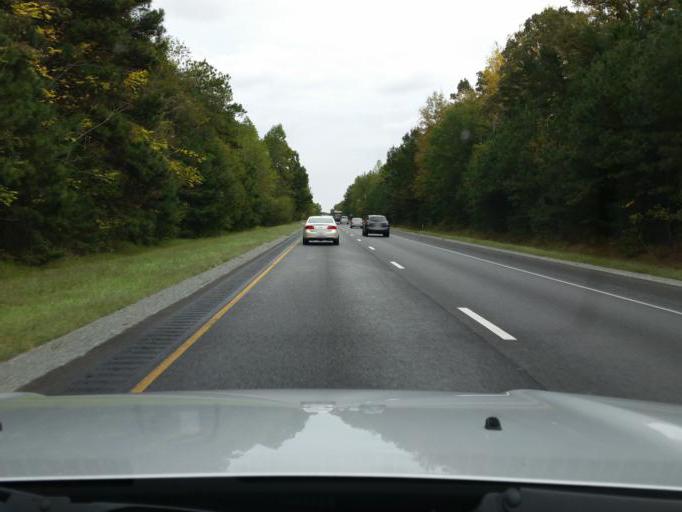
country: US
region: Virginia
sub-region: New Kent County
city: New Kent
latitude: 37.4909
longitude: -76.9910
